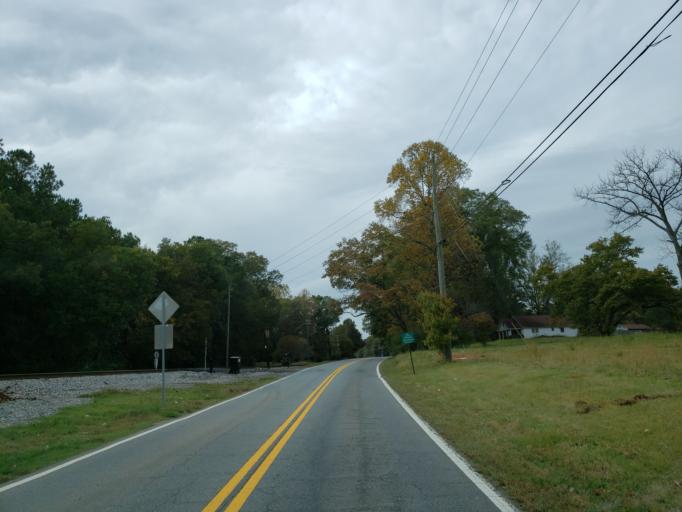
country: US
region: Georgia
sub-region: Cobb County
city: Acworth
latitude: 34.0631
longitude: -84.6573
